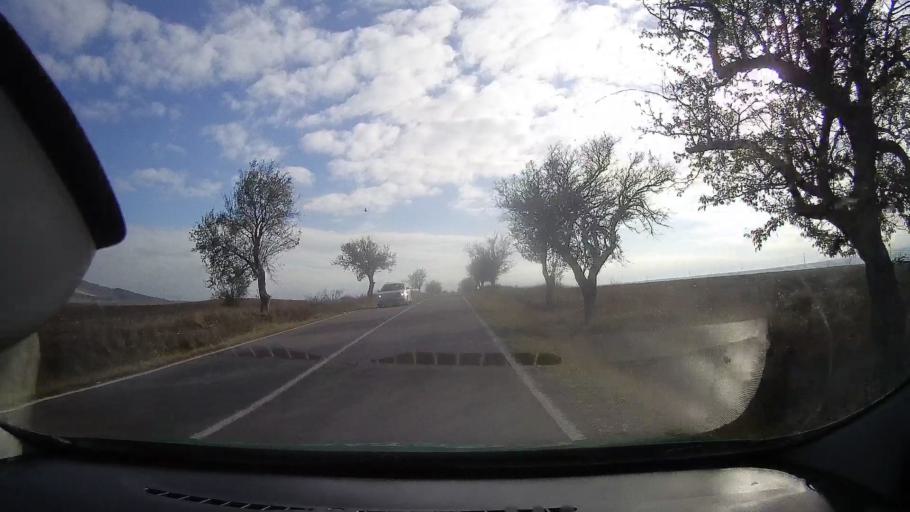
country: RO
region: Tulcea
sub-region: Comuna Bestepe
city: Bestepe
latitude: 45.0816
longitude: 29.0320
